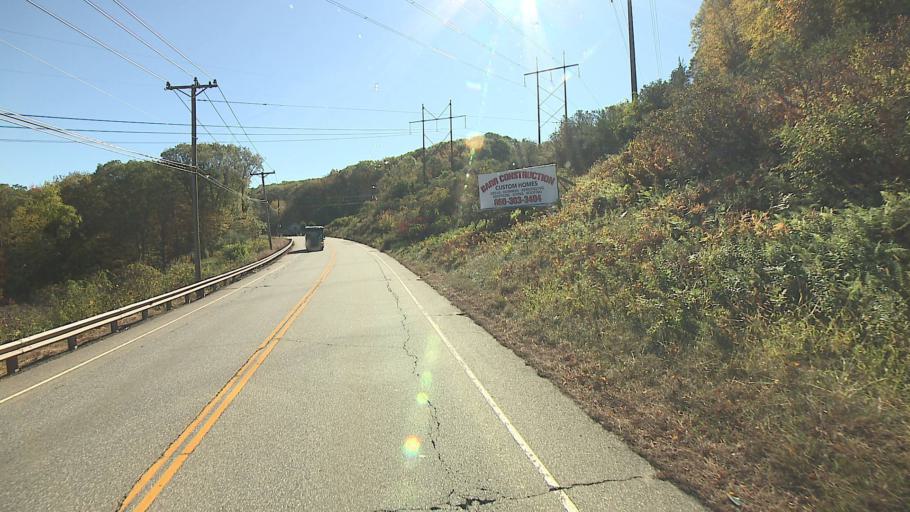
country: US
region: Connecticut
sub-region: Tolland County
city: Mansfield City
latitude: 41.7177
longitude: -72.2677
